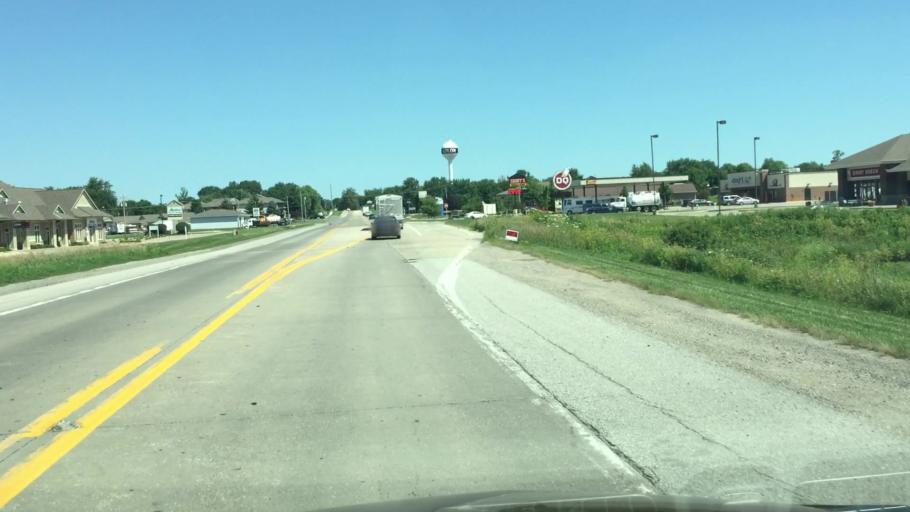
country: US
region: Iowa
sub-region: Johnson County
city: Solon
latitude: 41.7960
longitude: -91.4903
